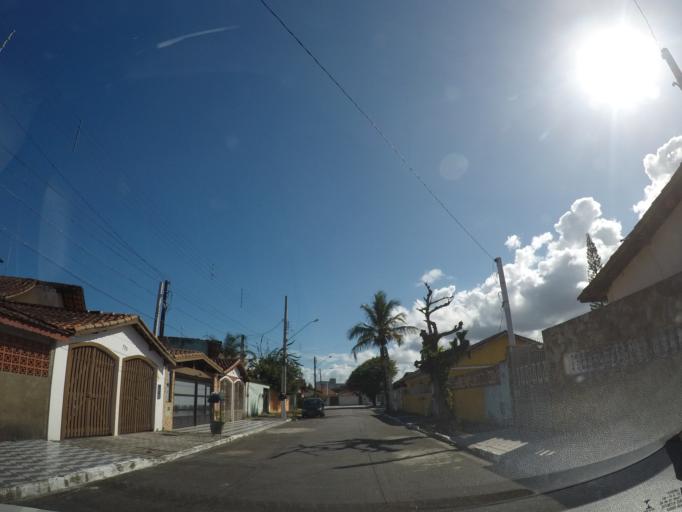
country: BR
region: Sao Paulo
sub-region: Mongagua
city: Mongagua
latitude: -24.0627
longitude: -46.5557
